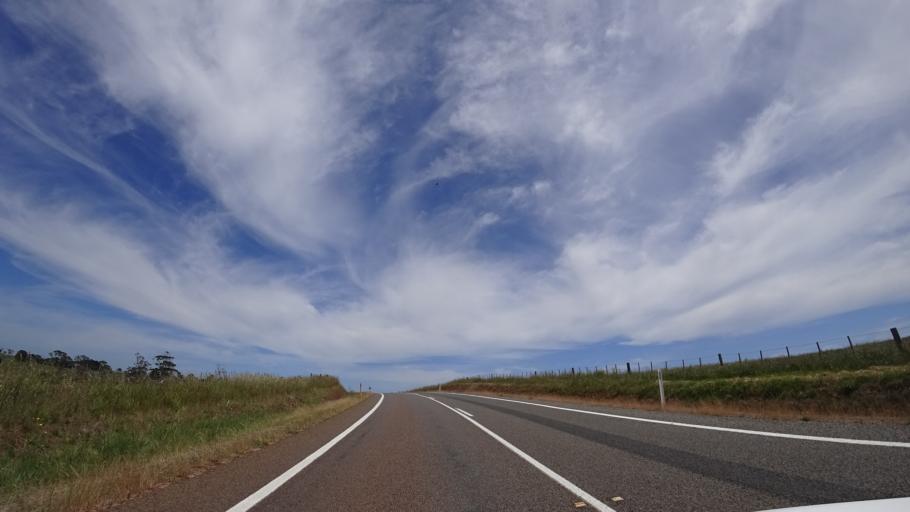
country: AU
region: Tasmania
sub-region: Dorset
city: Scottsdale
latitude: -41.1041
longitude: 147.8493
